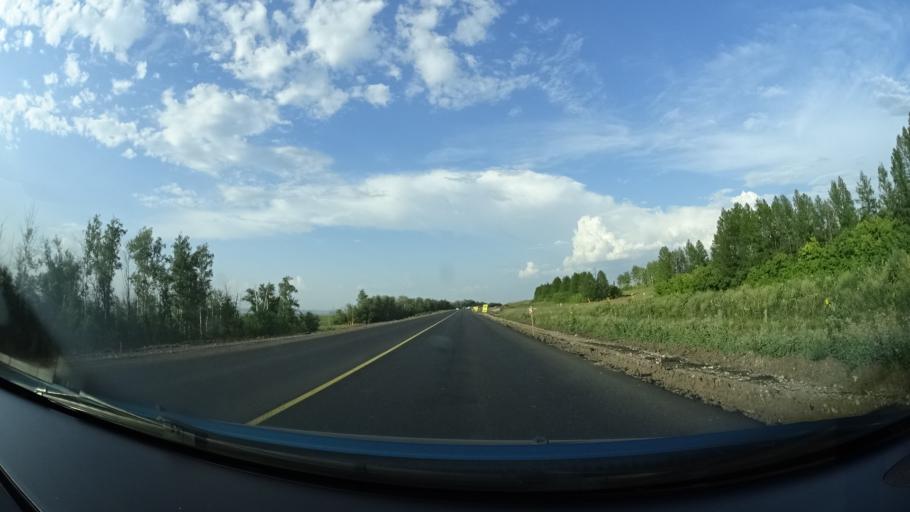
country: RU
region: Samara
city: Sukhodol
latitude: 53.7704
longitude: 50.8942
